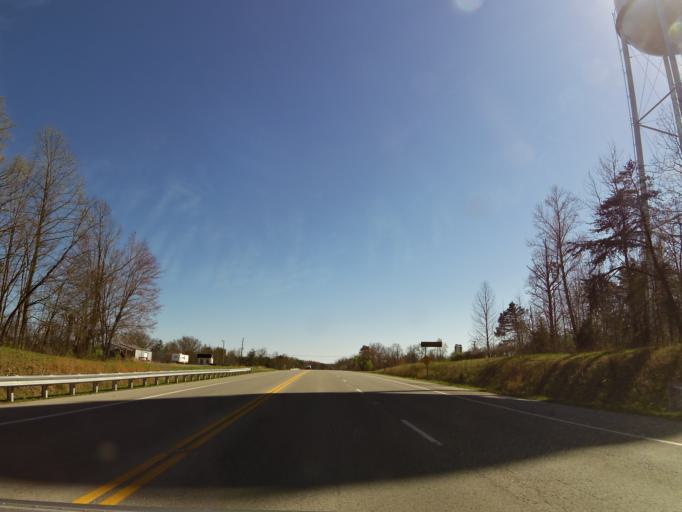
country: US
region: Kentucky
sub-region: McCreary County
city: Pine Knot
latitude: 36.6320
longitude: -84.4353
